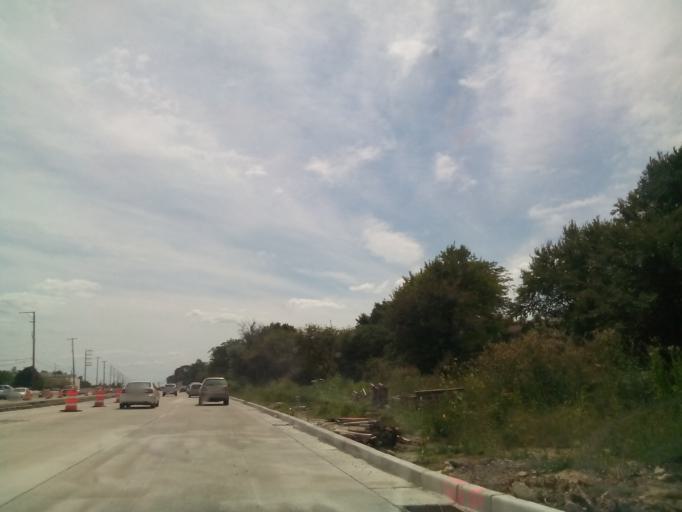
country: US
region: Illinois
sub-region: DuPage County
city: Warrenville
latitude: 41.7963
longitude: -88.2056
